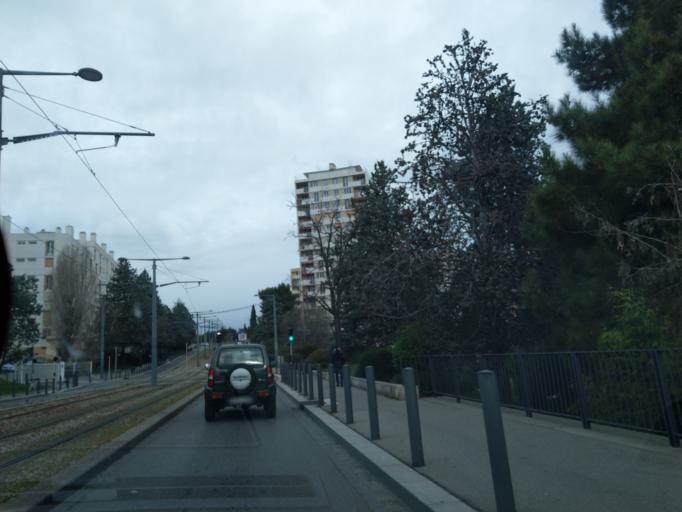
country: FR
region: Provence-Alpes-Cote d'Azur
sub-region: Departement des Bouches-du-Rhone
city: Marseille 12
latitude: 43.2929
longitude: 5.4349
